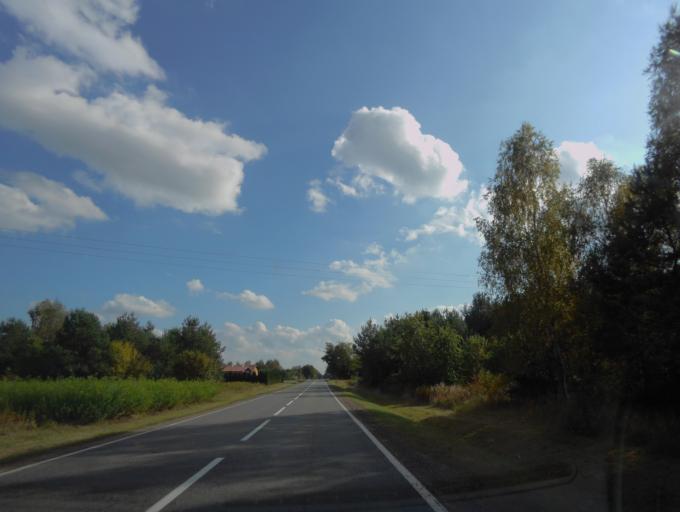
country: PL
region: Subcarpathian Voivodeship
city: Nowa Sarzyna
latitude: 50.3523
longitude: 22.3221
